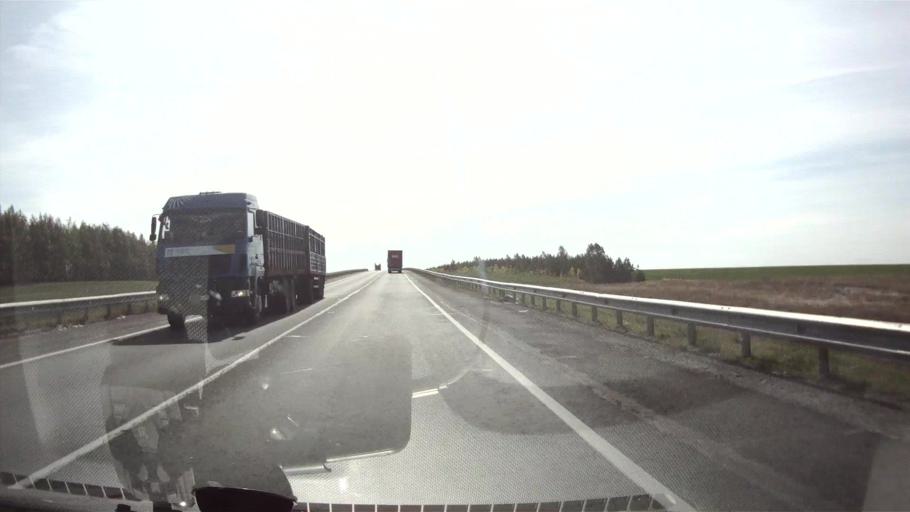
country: RU
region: Samara
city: Syzran'
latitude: 52.8994
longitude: 48.2960
